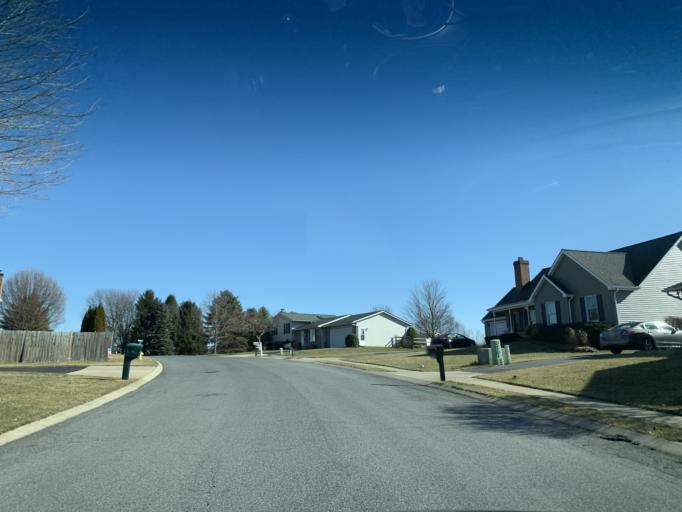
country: US
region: Maryland
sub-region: Carroll County
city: Westminster
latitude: 39.5953
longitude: -76.9940
